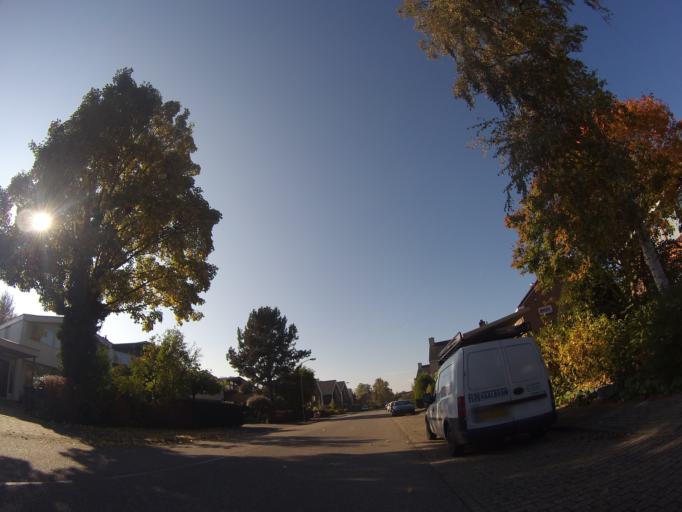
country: NL
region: Utrecht
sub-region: Gemeente Zeist
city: Zeist
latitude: 52.0501
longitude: 5.2376
